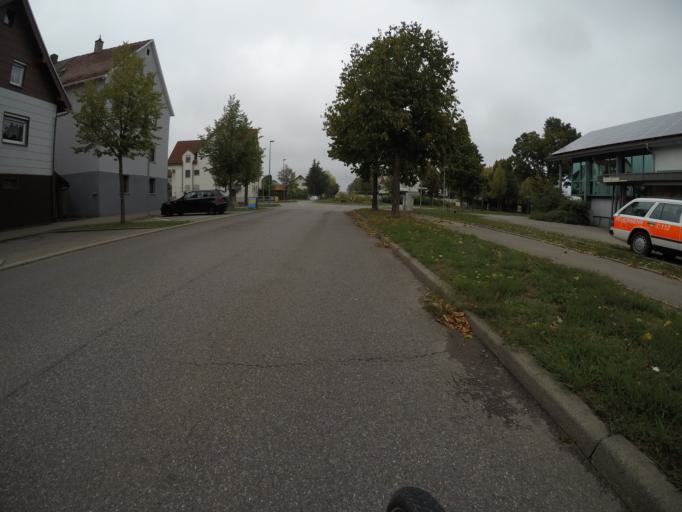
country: DE
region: Baden-Wuerttemberg
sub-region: Regierungsbezirk Stuttgart
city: Gartringen
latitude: 48.6426
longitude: 8.8941
